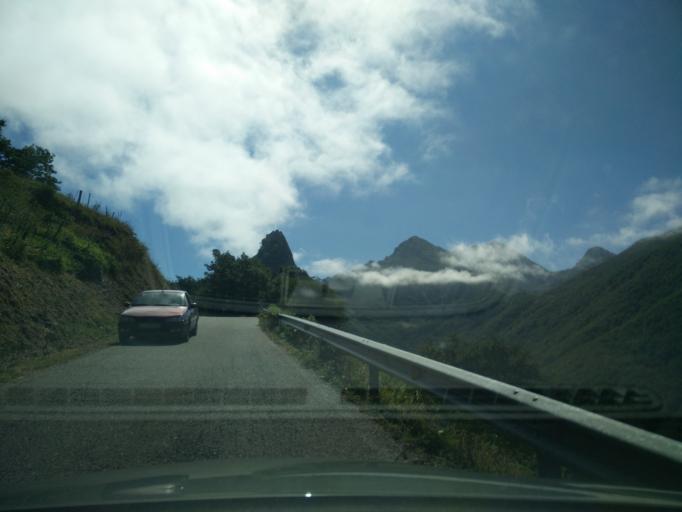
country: ES
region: Asturias
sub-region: Province of Asturias
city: Pola de Somiedo
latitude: 43.0736
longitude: -6.2188
